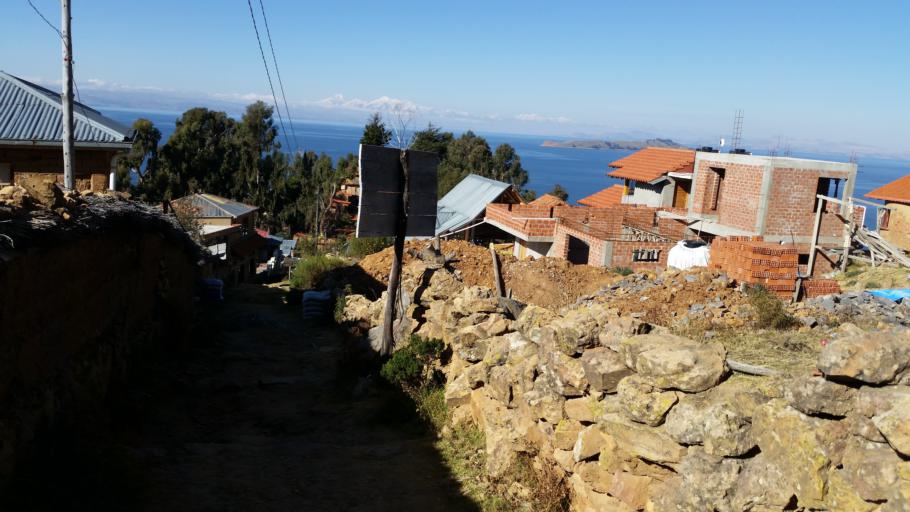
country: BO
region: La Paz
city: Yumani
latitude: -16.0371
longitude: -69.1475
